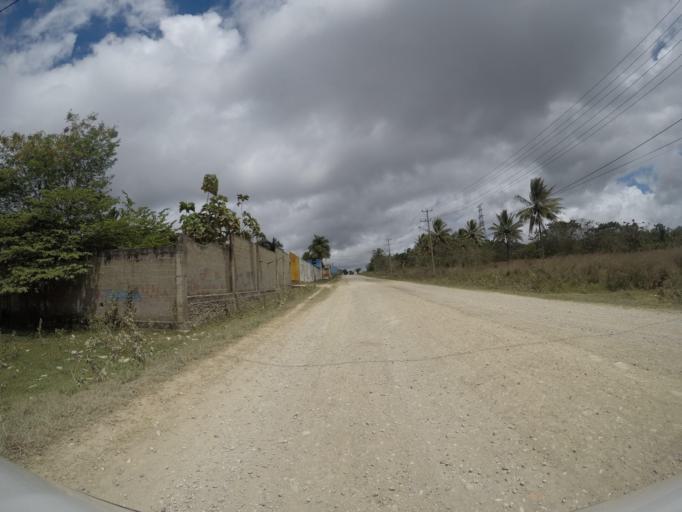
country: TL
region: Lautem
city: Lospalos
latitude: -8.4898
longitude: 126.9927
